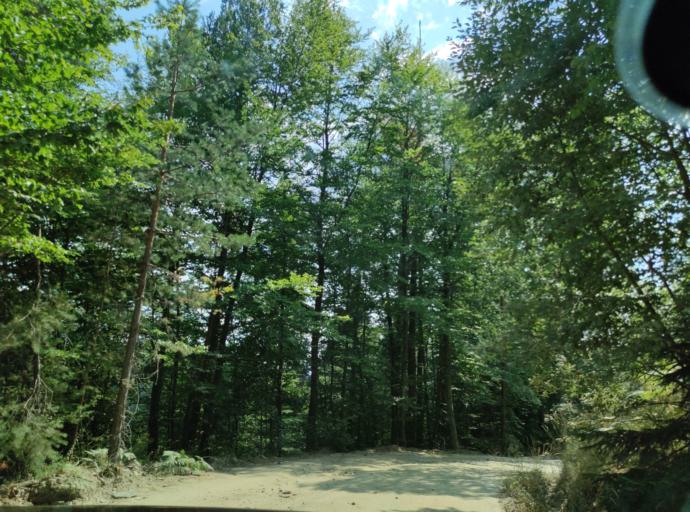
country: BG
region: Blagoevgrad
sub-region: Obshtina Belitsa
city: Belitsa
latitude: 42.0268
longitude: 23.5820
